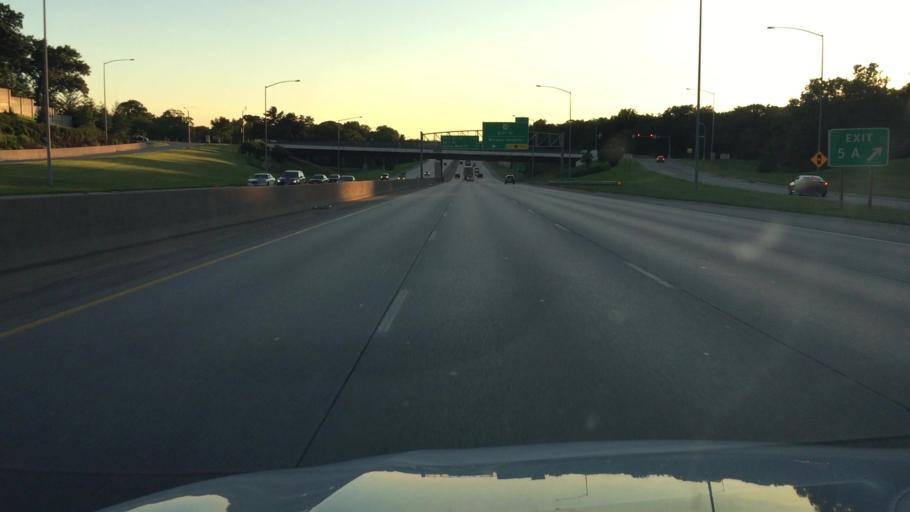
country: US
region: Iowa
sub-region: Polk County
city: Windsor Heights
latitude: 41.5925
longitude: -93.6909
